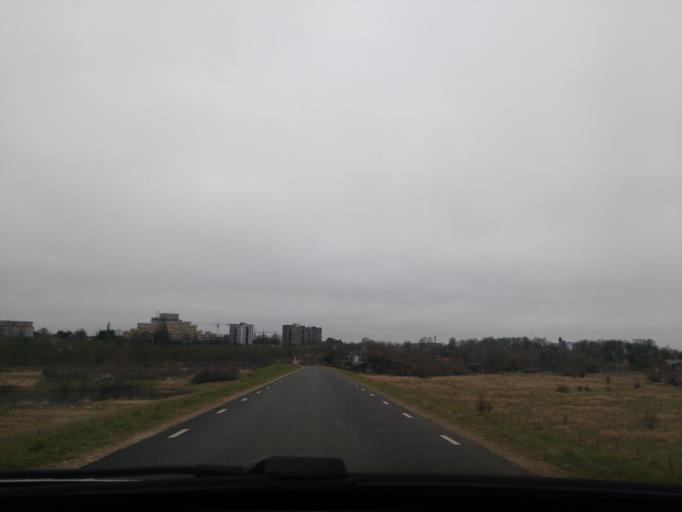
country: NL
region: Gelderland
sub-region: Gemeente Nijmegen
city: Nijmegen
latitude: 51.8498
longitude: 5.8841
